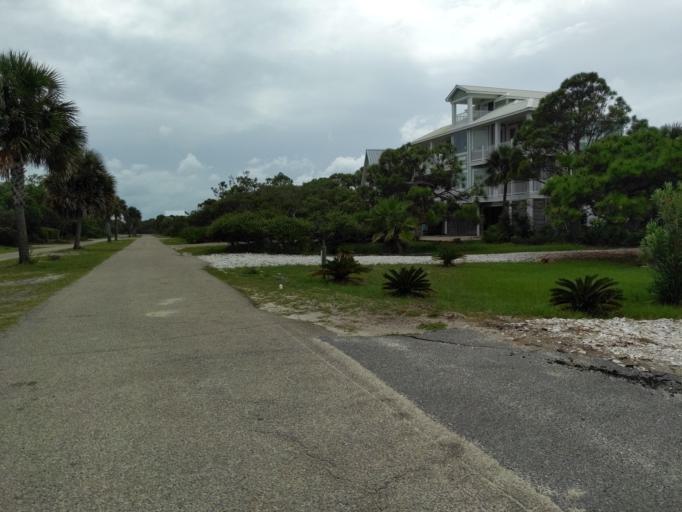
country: US
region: Florida
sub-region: Franklin County
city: Apalachicola
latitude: 29.6276
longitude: -84.9316
